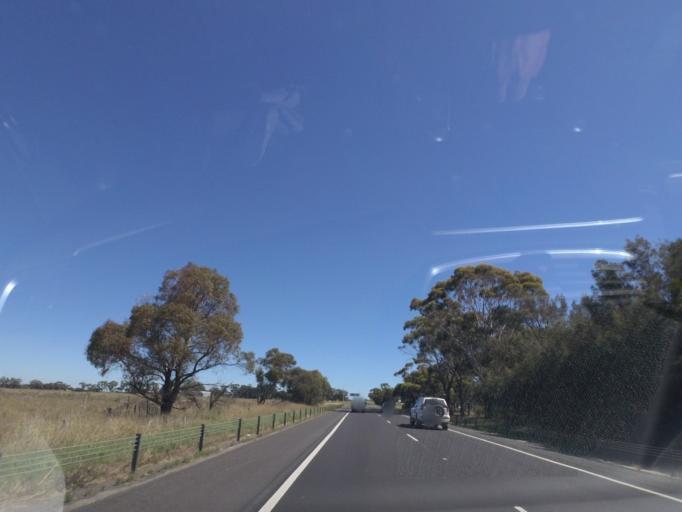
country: AU
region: Victoria
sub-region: Hume
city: Craigieburn
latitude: -37.5583
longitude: 144.9428
